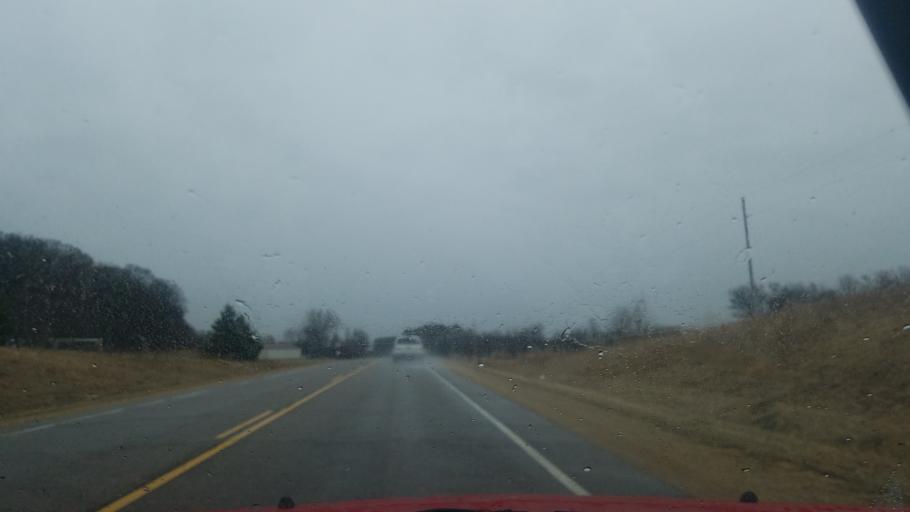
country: US
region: Wisconsin
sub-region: Dunn County
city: Tainter Lake
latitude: 45.0192
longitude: -91.8913
